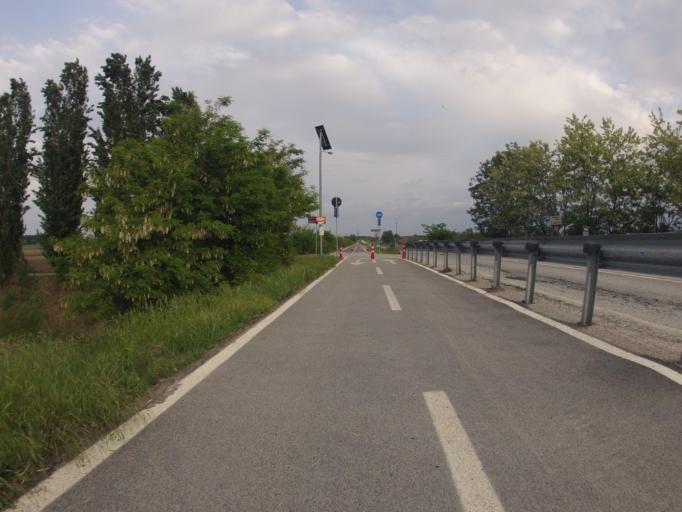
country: IT
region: Piedmont
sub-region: Provincia di Torino
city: Villafranca Piemonte
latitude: 44.7790
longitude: 7.5136
